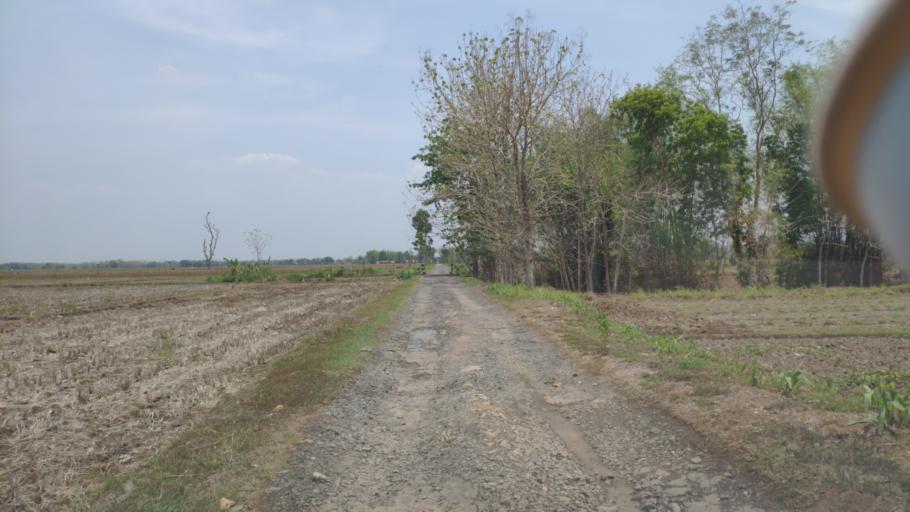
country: ID
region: Central Java
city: Plumbon
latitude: -7.0525
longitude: 111.2992
